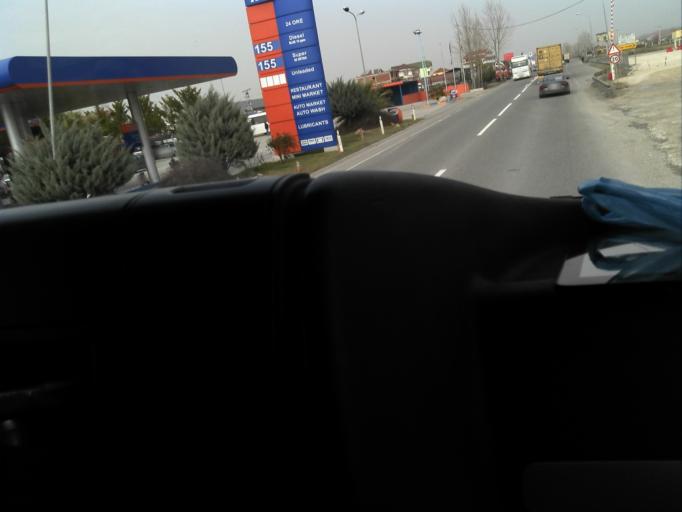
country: AL
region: Tirane
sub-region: Rrethi i Tiranes
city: Preze
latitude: 41.4316
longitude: 19.6880
